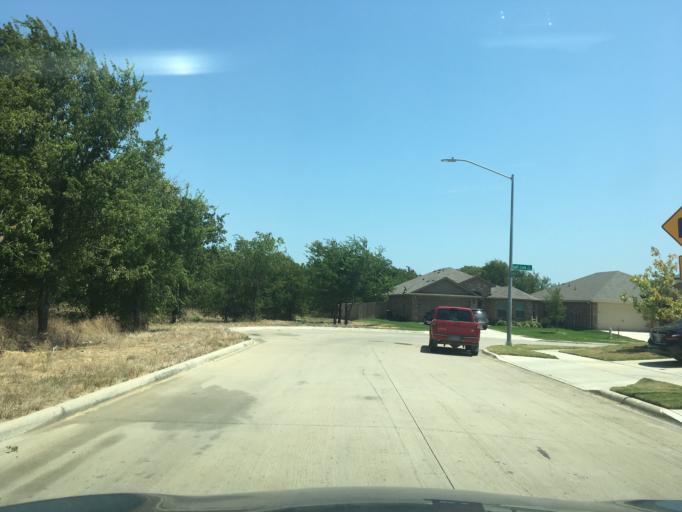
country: US
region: Texas
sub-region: Tarrant County
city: Crowley
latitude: 32.6142
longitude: -97.3596
